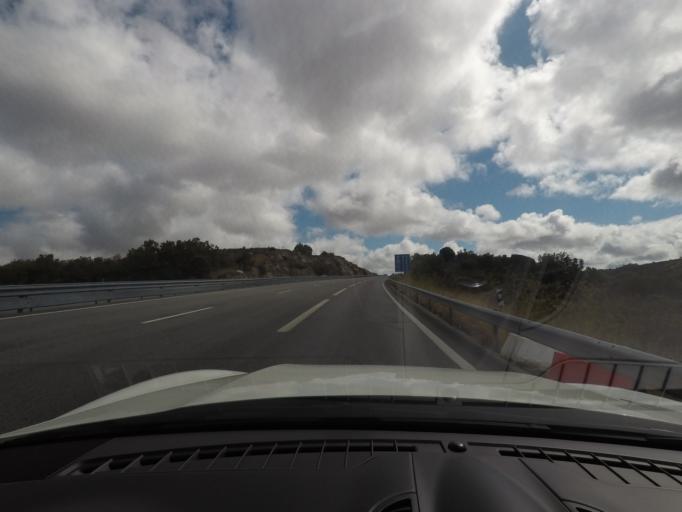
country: ES
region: Castille and Leon
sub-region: Provincia de Salamanca
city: Fuentes de Onoro
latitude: 40.6117
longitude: -6.9123
